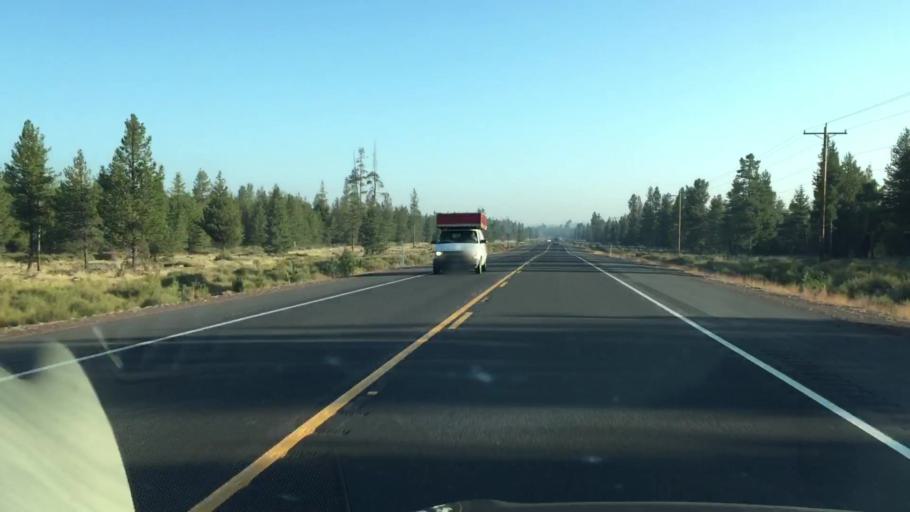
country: US
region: Oregon
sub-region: Deschutes County
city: La Pine
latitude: 43.1918
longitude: -121.7806
